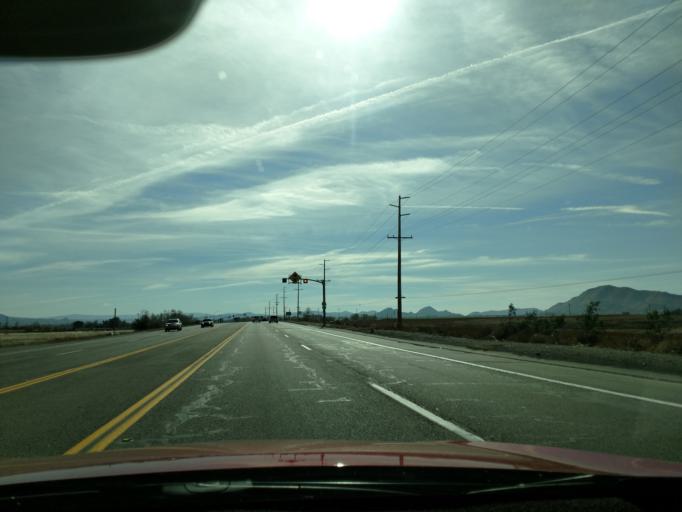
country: US
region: California
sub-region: Riverside County
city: San Jacinto
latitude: 33.8273
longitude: -117.0036
